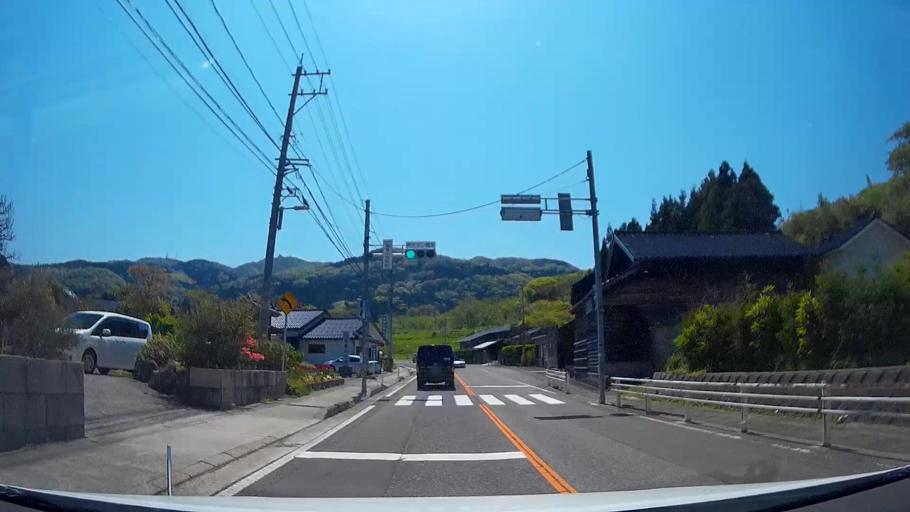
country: JP
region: Ishikawa
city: Nanao
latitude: 37.3967
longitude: 136.9339
